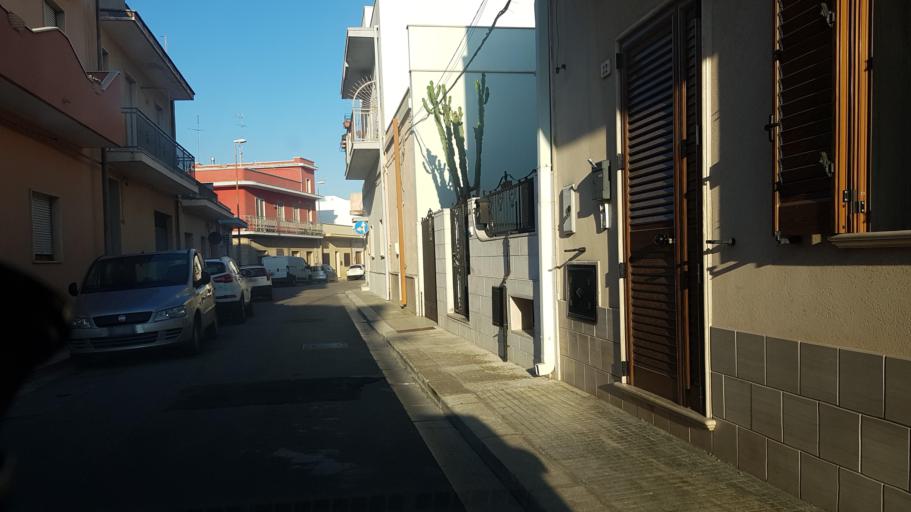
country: IT
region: Apulia
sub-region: Provincia di Brindisi
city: Mesagne
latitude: 40.5610
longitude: 17.8146
